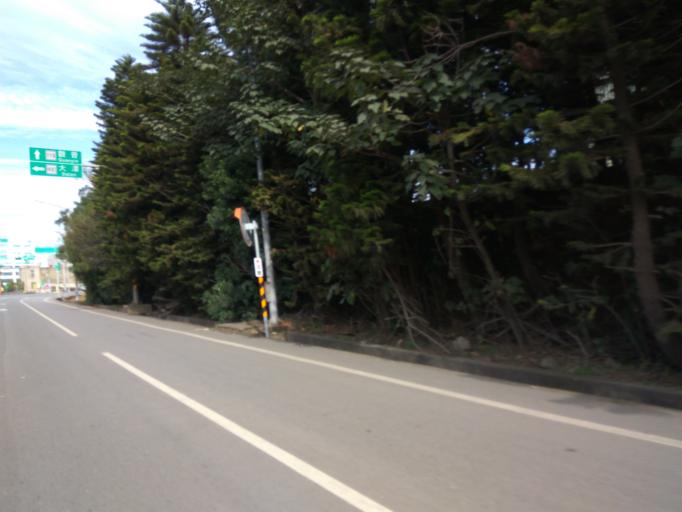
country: TW
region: Taiwan
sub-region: Hsinchu
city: Zhubei
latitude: 24.9895
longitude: 121.1024
